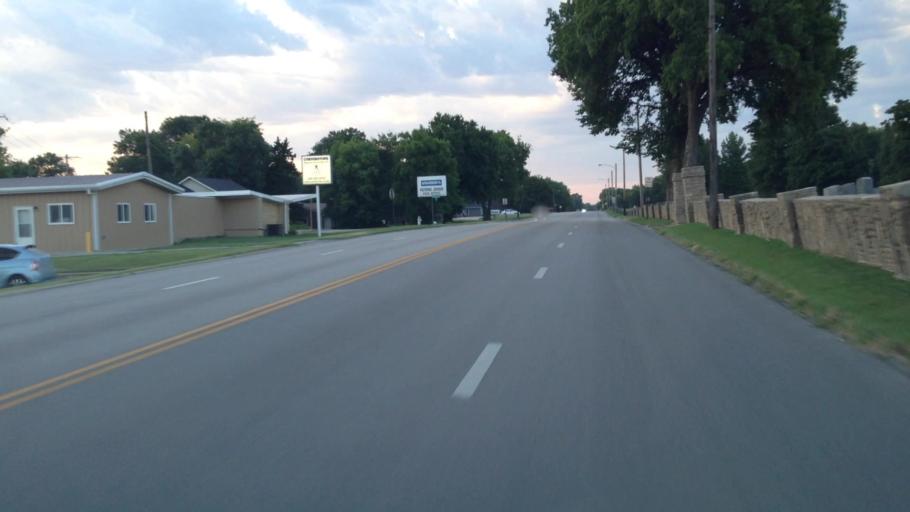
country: US
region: Kansas
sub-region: Montgomery County
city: Independence
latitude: 37.2438
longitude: -95.7062
